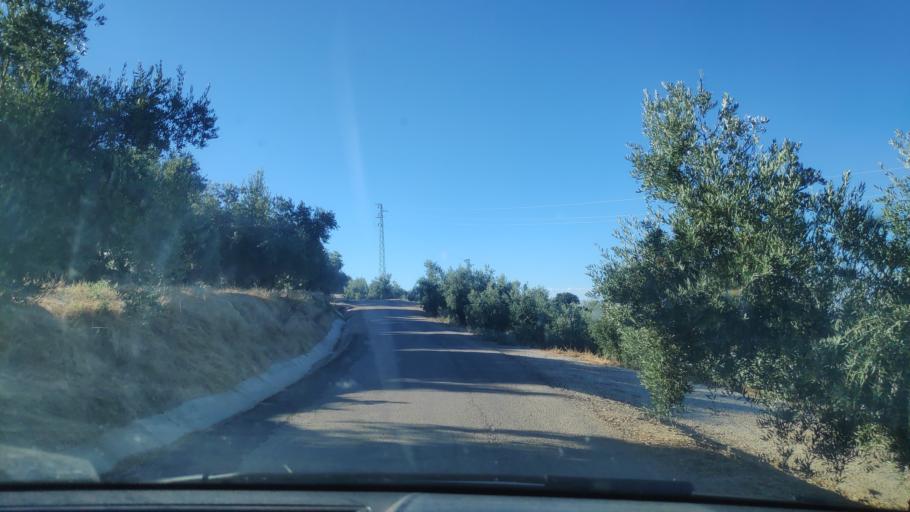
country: ES
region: Andalusia
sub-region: Provincia de Jaen
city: Torres
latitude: 37.7816
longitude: -3.5411
